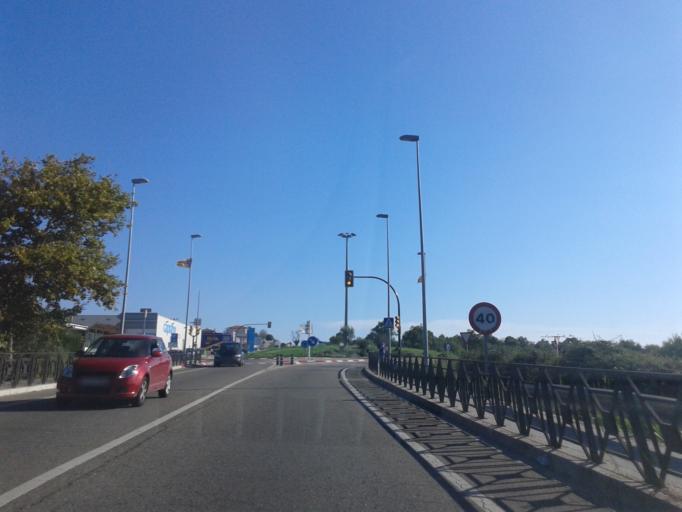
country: ES
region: Catalonia
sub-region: Provincia de Tarragona
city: El Vendrell
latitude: 41.2179
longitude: 1.5450
